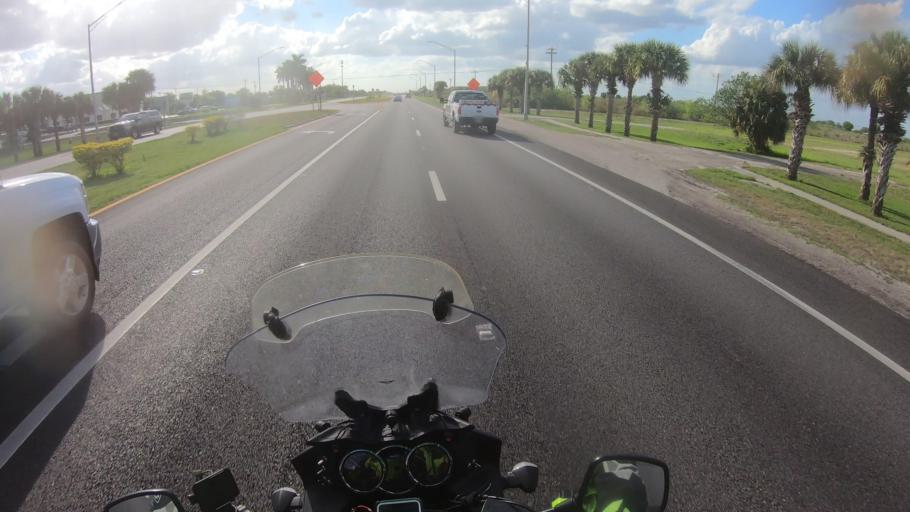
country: US
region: Florida
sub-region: Glades County
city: Moore Haven
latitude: 26.8351
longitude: -81.1070
